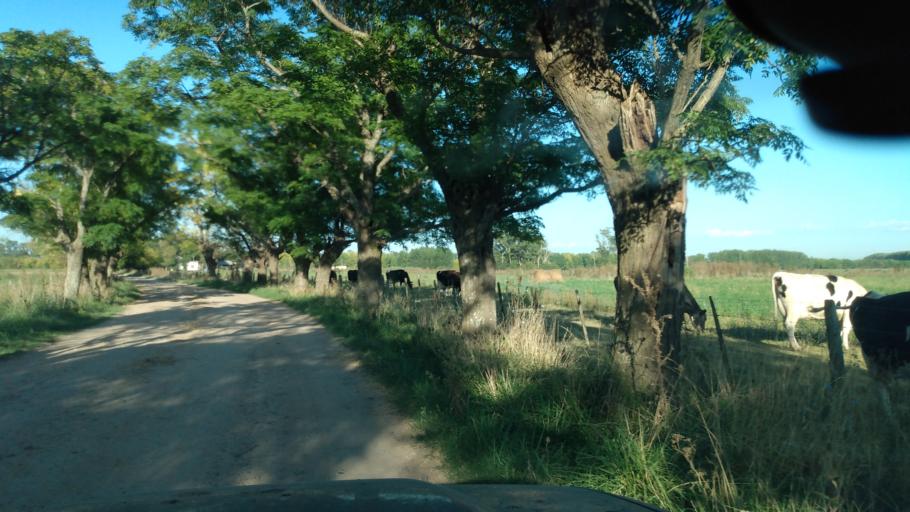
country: AR
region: Buenos Aires
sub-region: Partido de Lujan
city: Lujan
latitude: -34.5873
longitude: -59.0684
